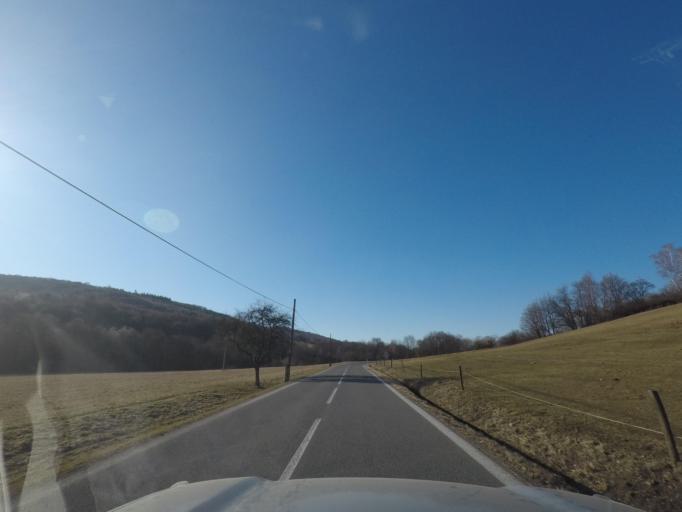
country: SK
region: Presovsky
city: Medzilaborce
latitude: 49.1812
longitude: 22.0158
